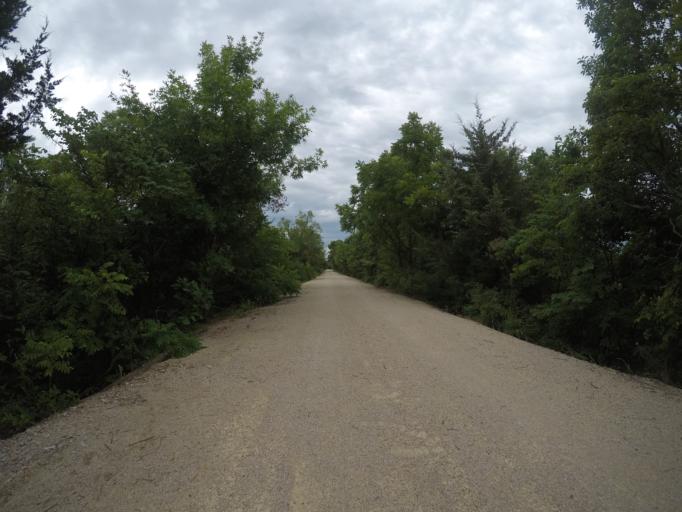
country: US
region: Kansas
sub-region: Anderson County
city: Garnett
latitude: 38.3087
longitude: -95.2474
